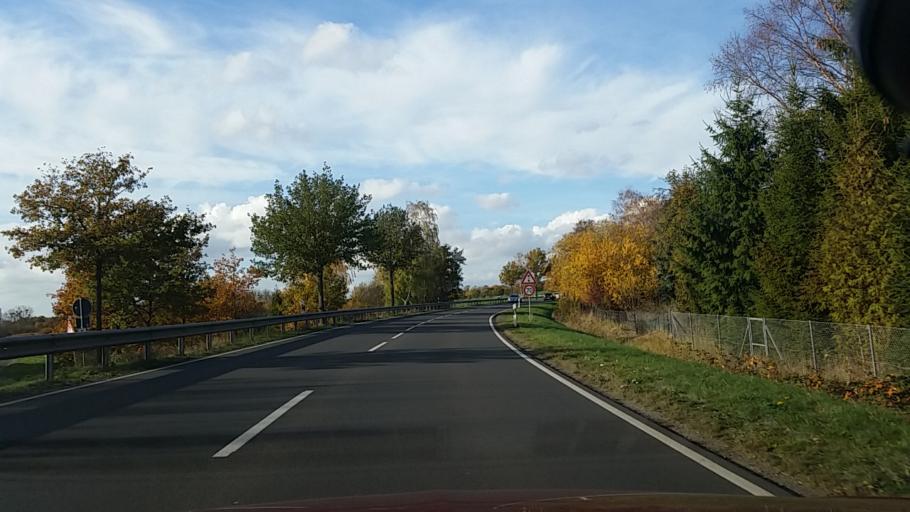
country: DE
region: Lower Saxony
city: Wolfsburg
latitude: 52.4367
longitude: 10.8321
